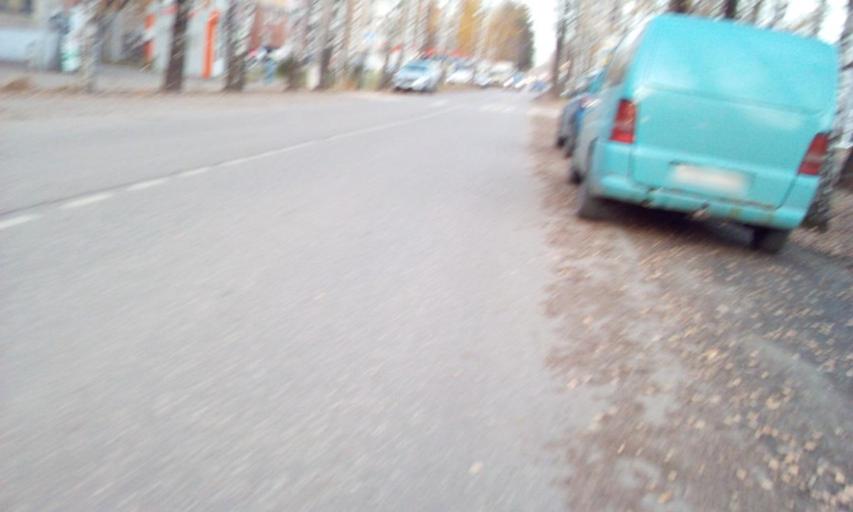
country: RU
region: Moskovskaya
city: Aprelevka
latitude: 55.5528
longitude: 37.0716
